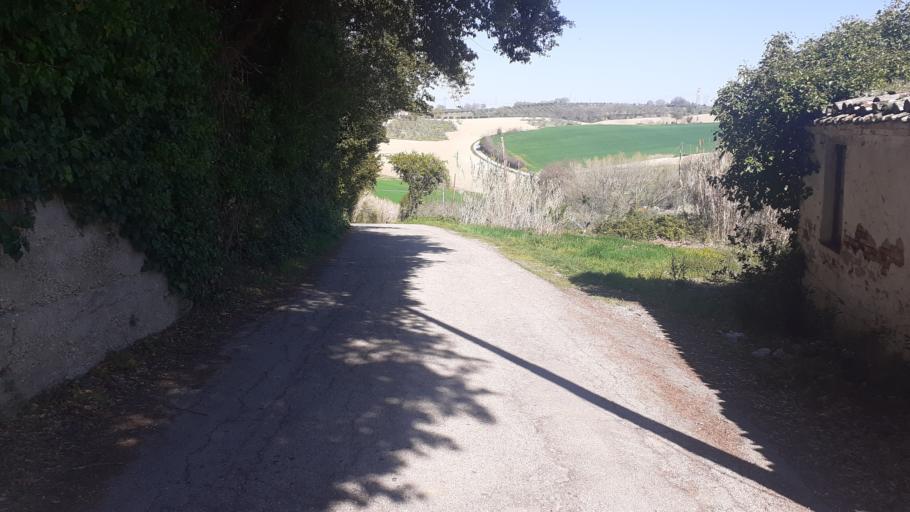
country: IT
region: Abruzzo
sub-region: Provincia di Pescara
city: Cerratina
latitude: 42.3966
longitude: 14.1129
